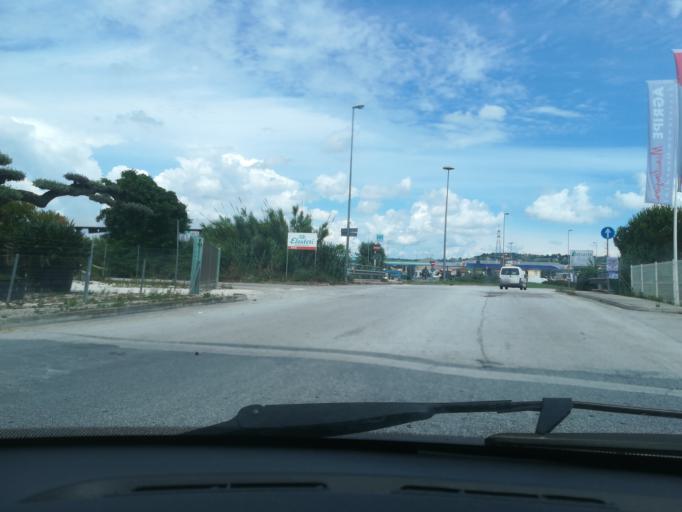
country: IT
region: The Marches
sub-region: Provincia di Macerata
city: Santa Maria Apparente
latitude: 43.2812
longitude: 13.6847
